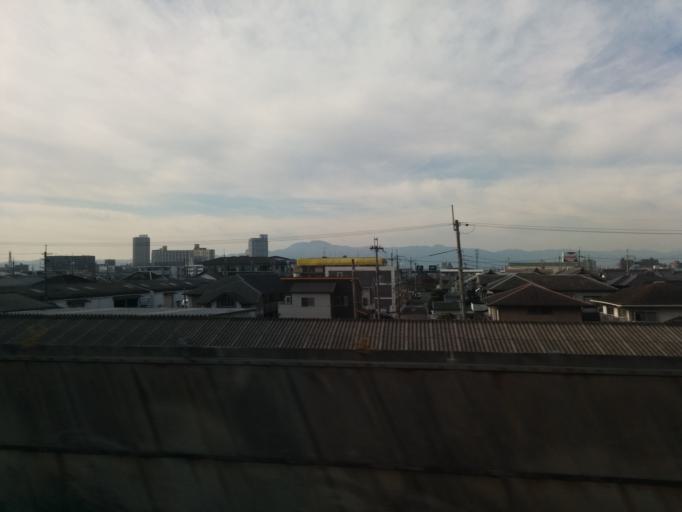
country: JP
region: Shiga Prefecture
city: Kusatsu
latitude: 35.0188
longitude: 135.9794
